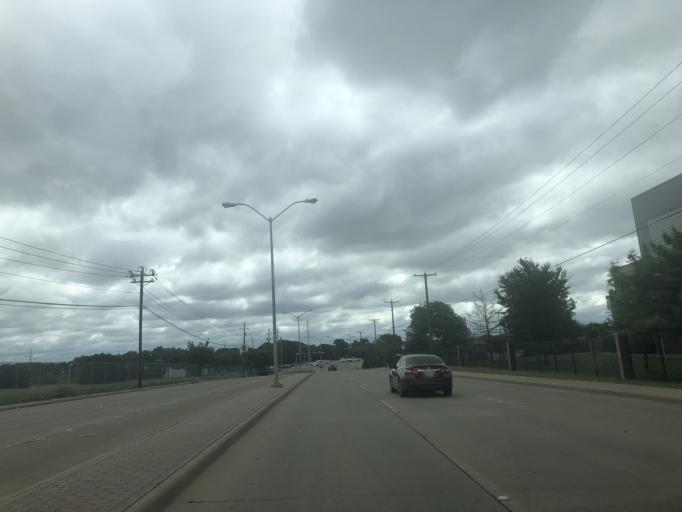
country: US
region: Texas
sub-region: Dallas County
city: Duncanville
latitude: 32.6624
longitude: -96.9290
